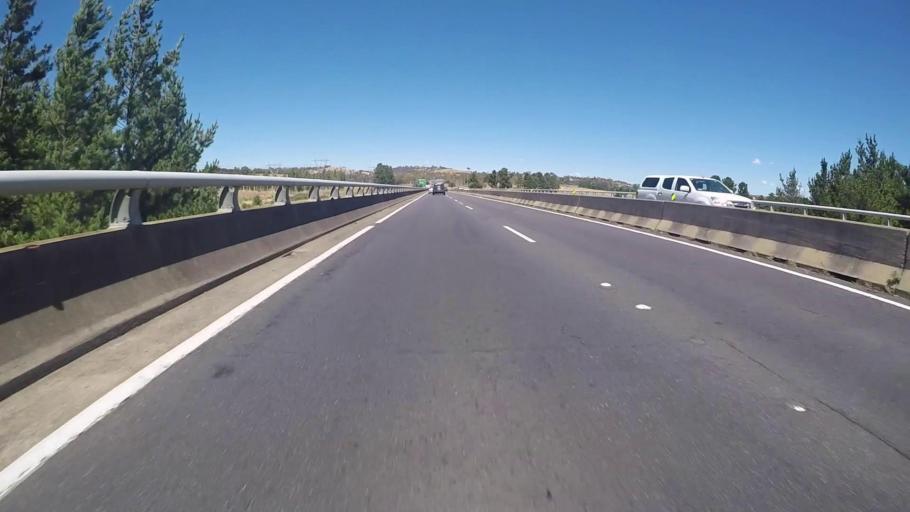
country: AU
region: Australian Capital Territory
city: Macquarie
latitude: -35.3130
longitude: 149.0624
